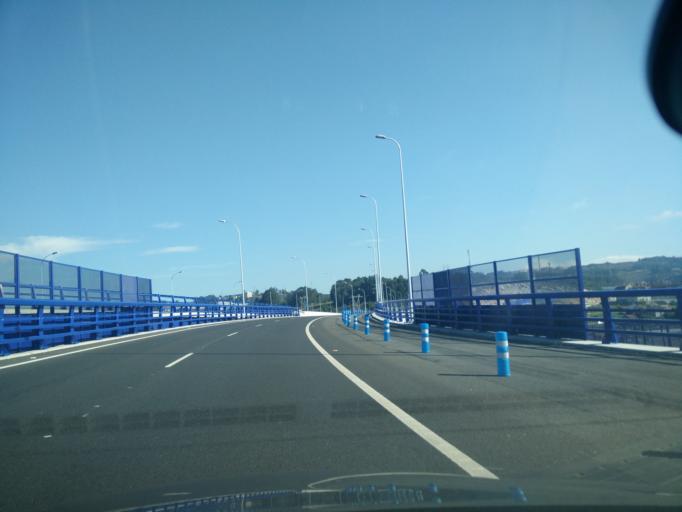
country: ES
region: Galicia
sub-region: Provincia da Coruna
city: A Coruna
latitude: 43.3382
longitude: -8.4233
